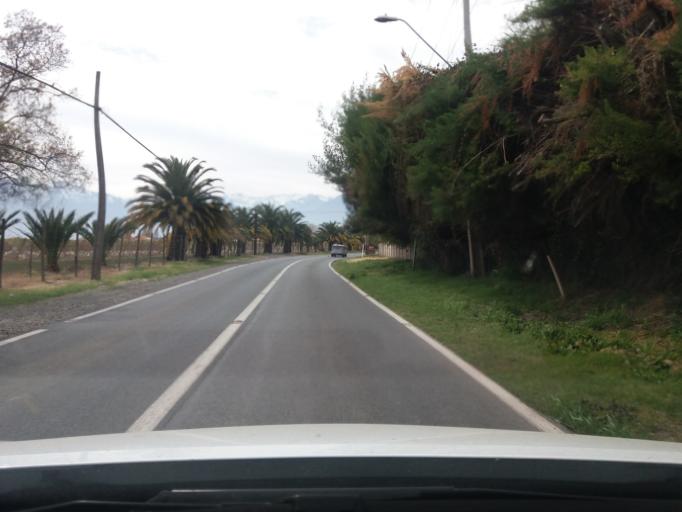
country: CL
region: Valparaiso
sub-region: Provincia de Los Andes
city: Los Andes
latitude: -32.8325
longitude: -70.6261
